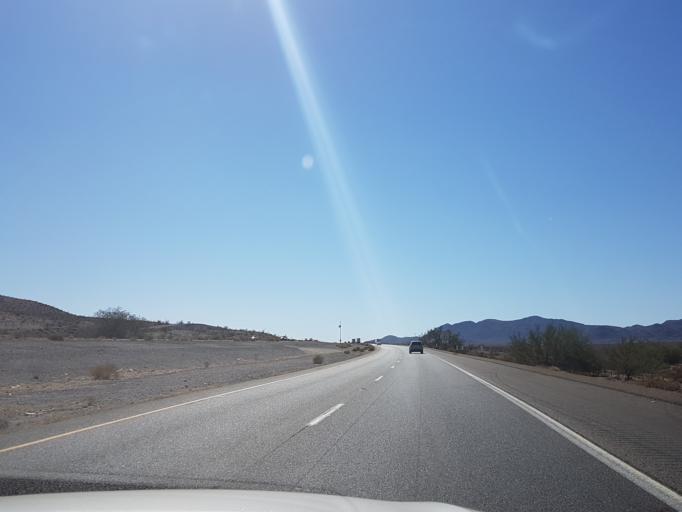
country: US
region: California
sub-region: San Bernardino County
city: Fort Irwin
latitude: 35.1883
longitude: -116.1610
